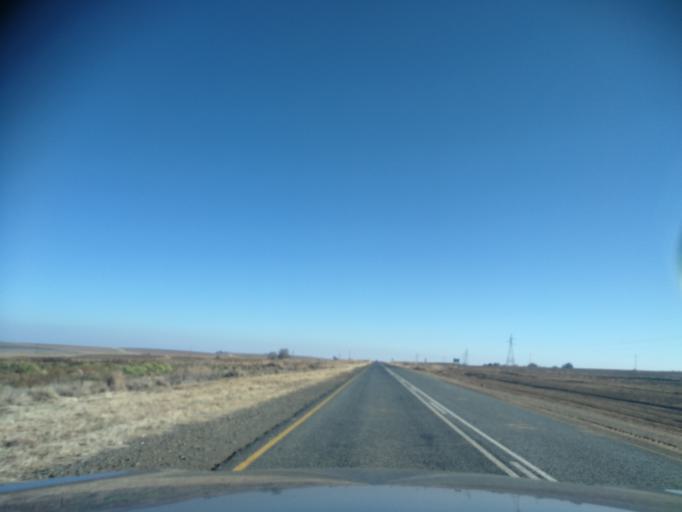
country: ZA
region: Orange Free State
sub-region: Thabo Mofutsanyana District Municipality
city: Bethlehem
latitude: -28.1143
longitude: 28.1944
